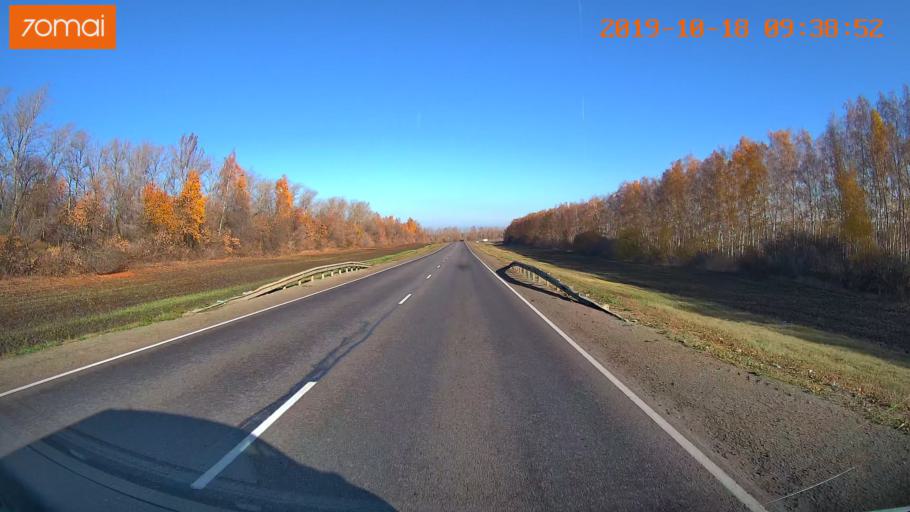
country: RU
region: Tula
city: Yefremov
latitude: 53.2446
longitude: 38.1353
